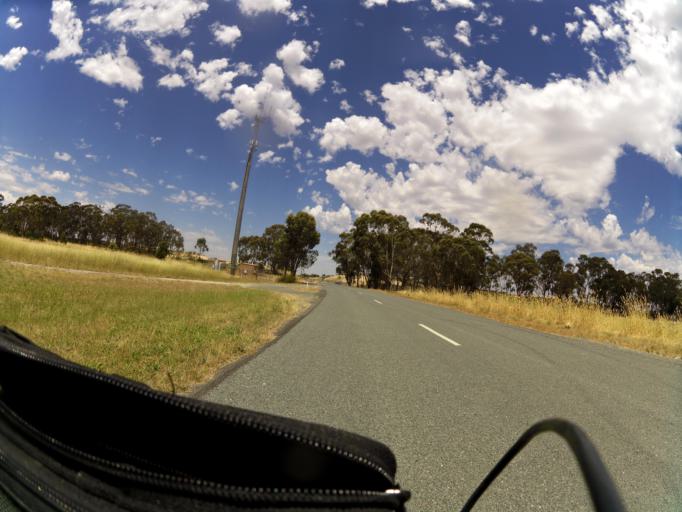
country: AU
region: Victoria
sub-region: Greater Shepparton
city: Shepparton
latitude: -36.6288
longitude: 145.2111
